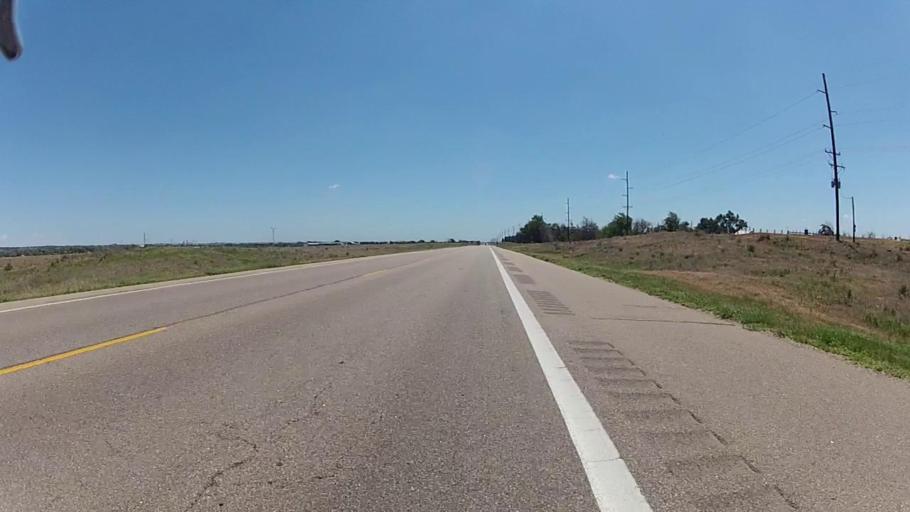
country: US
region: Kansas
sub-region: Ford County
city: Dodge City
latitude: 37.7223
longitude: -100.0435
